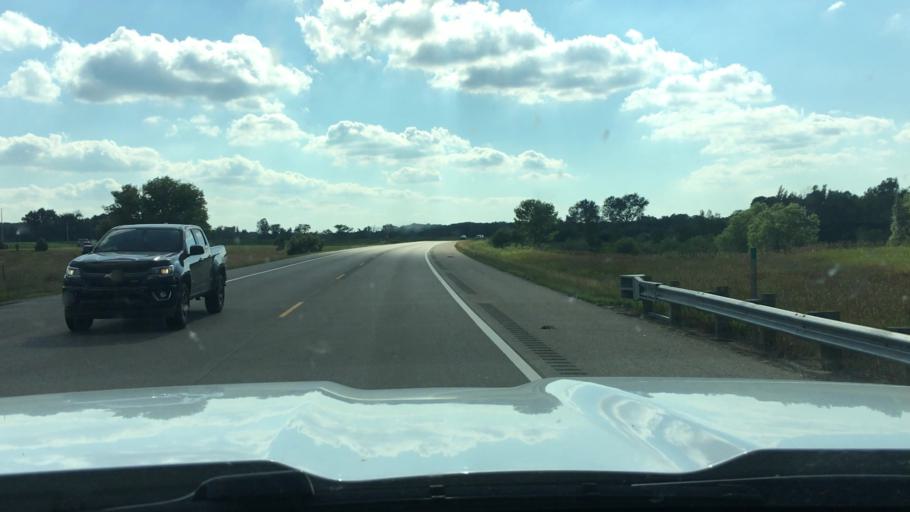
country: US
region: Michigan
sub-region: Ionia County
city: Belding
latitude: 43.0821
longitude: -85.3724
